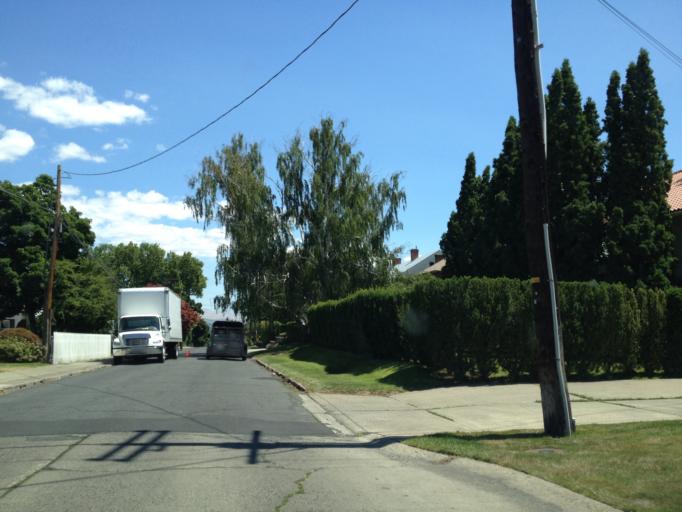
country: US
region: Washington
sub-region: Yakima County
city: Yakima
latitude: 46.5971
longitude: -120.5360
